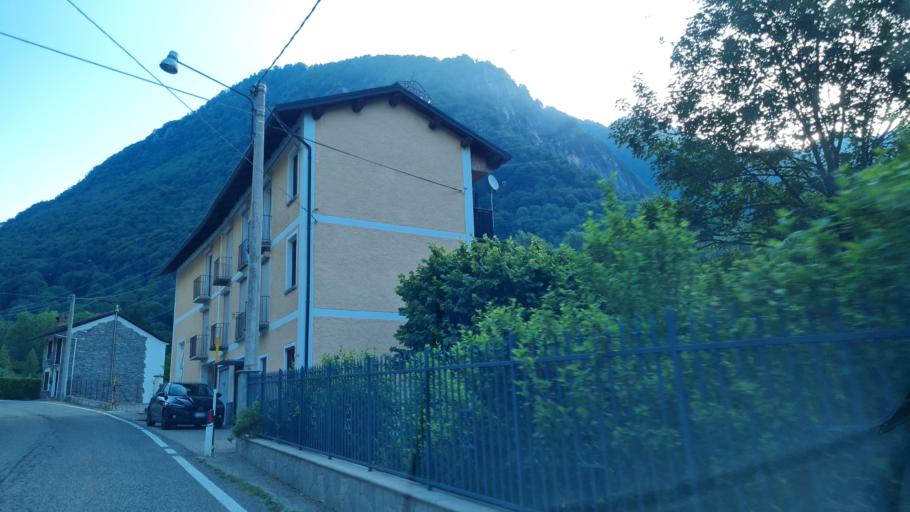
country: IT
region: Piedmont
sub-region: Provincia di Torino
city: Ronco Canavese
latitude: 45.5081
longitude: 7.5515
